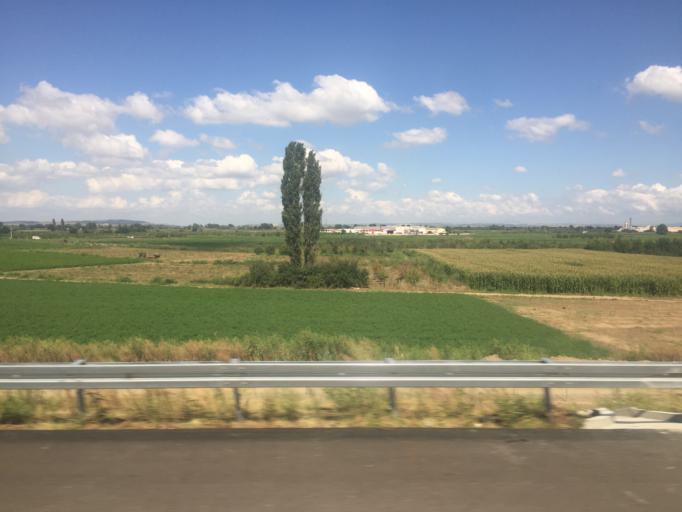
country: TR
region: Balikesir
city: Gobel
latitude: 40.0631
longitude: 28.2436
